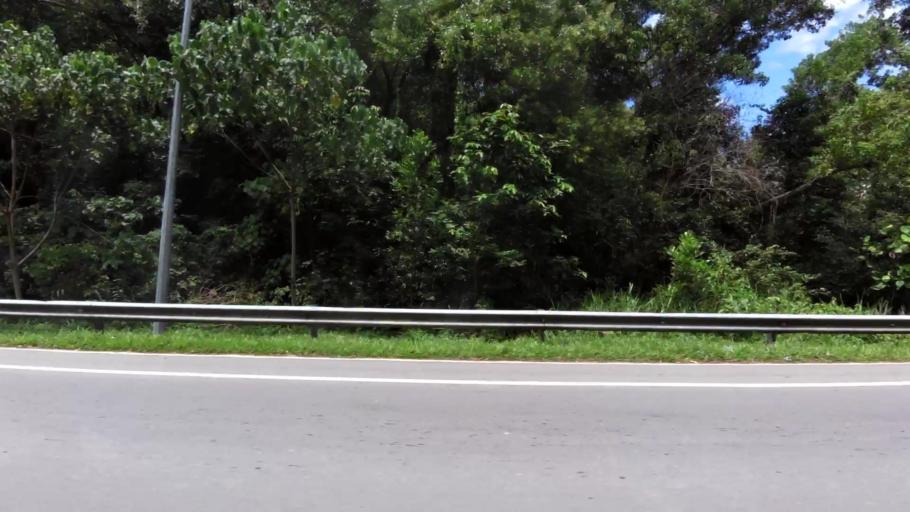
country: BN
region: Brunei and Muara
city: Bandar Seri Begawan
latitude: 4.9951
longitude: 115.0195
